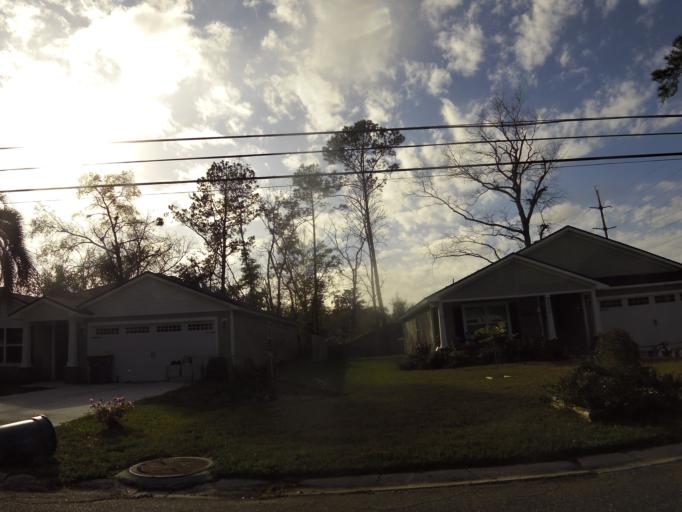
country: US
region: Florida
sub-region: Duval County
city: Jacksonville
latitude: 30.2858
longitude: -81.6135
